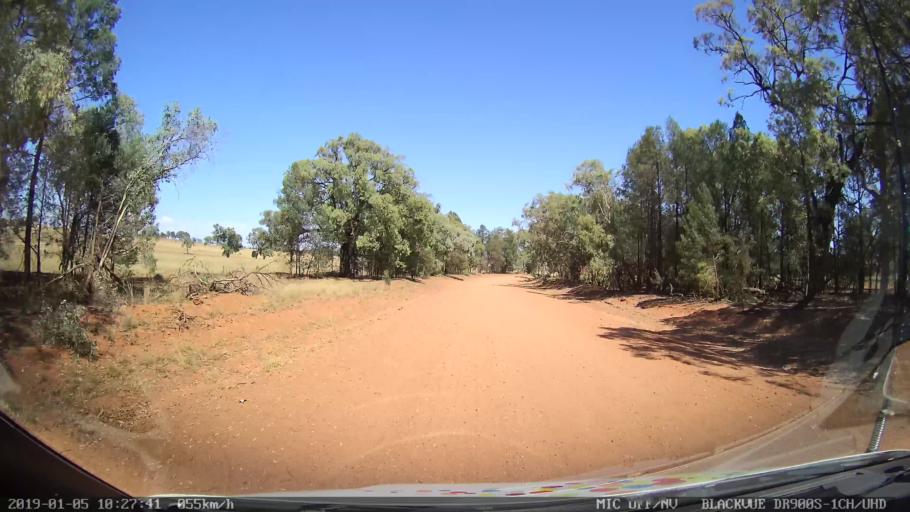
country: AU
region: New South Wales
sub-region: Gilgandra
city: Gilgandra
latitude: -31.5491
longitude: 148.9444
